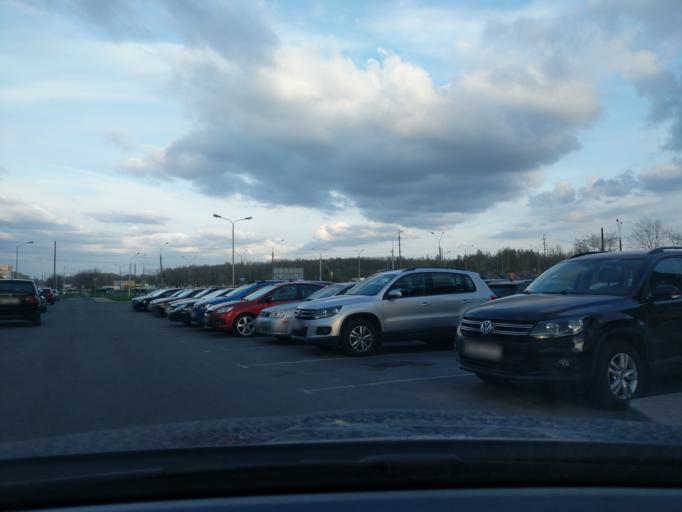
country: BY
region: Minsk
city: Novoye Medvezhino
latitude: 53.8938
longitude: 27.4609
